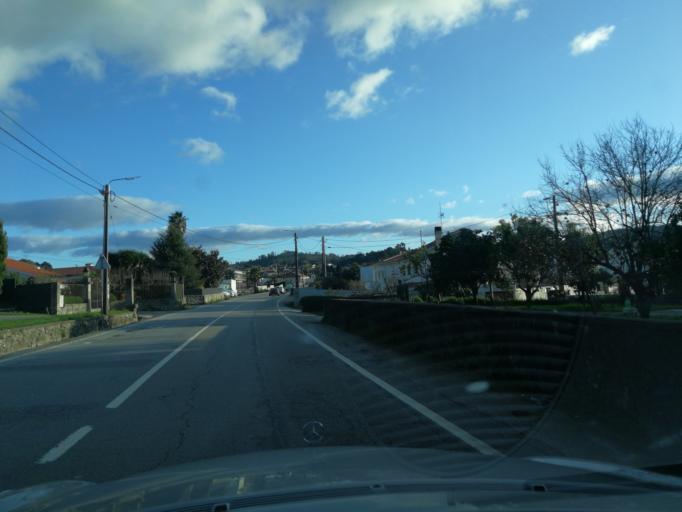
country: PT
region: Braga
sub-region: Esposende
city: Marinhas
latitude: 41.6117
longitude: -8.7414
